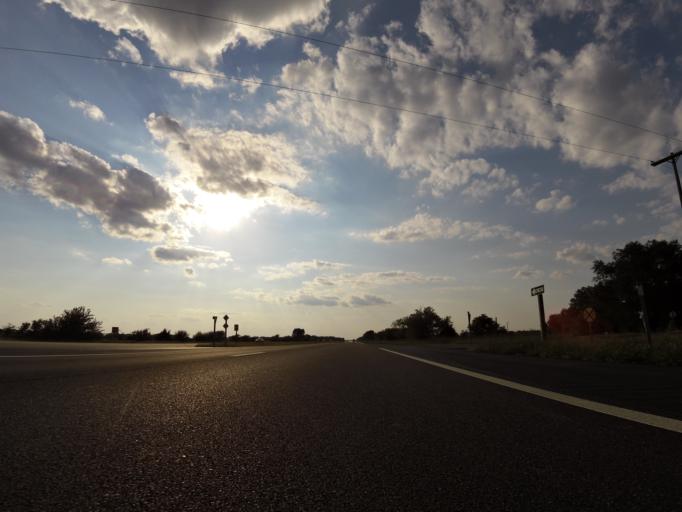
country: US
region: Kansas
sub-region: Reno County
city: Haven
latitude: 37.8819
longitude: -97.7193
